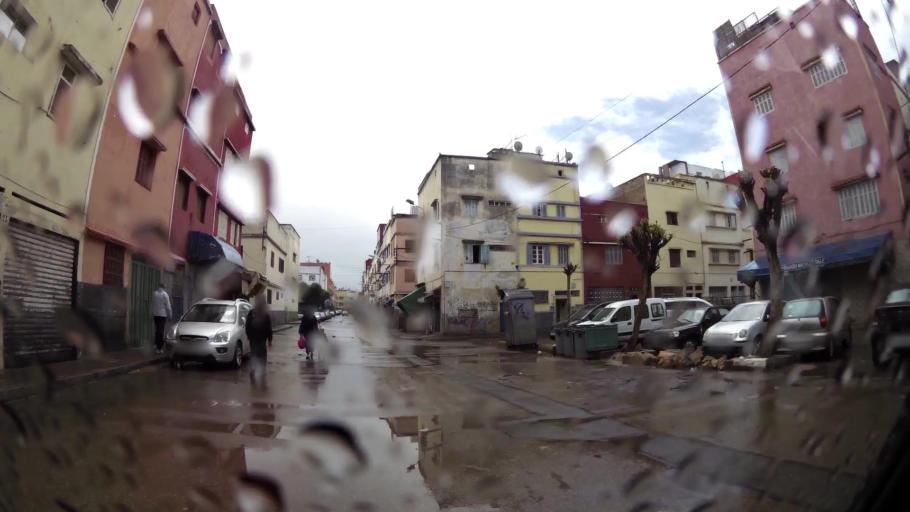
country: MA
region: Grand Casablanca
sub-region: Casablanca
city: Casablanca
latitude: 33.5715
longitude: -7.5946
